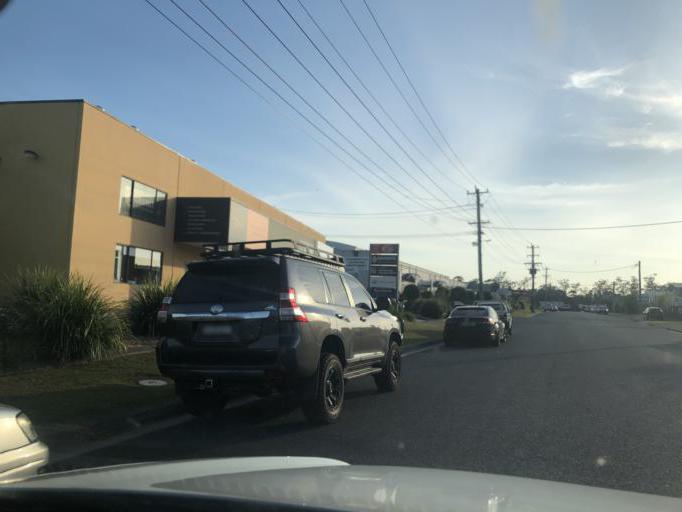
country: AU
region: New South Wales
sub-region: Coffs Harbour
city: Boambee
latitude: -30.3176
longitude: 153.0850
